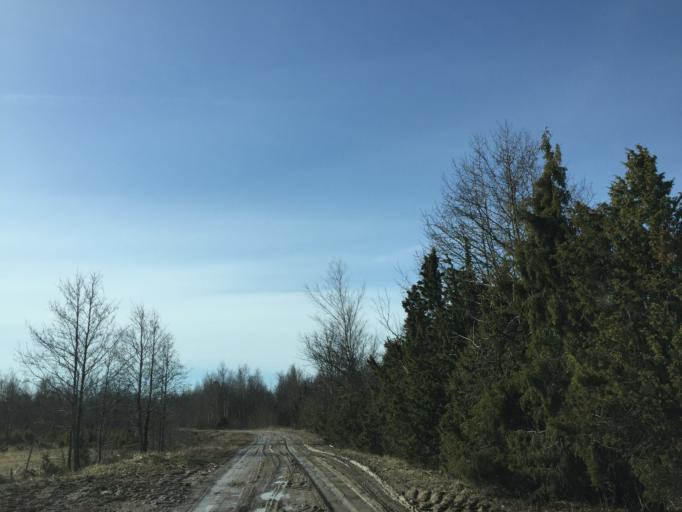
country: EE
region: Laeaene
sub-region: Haapsalu linn
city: Haapsalu
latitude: 58.6588
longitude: 23.5140
